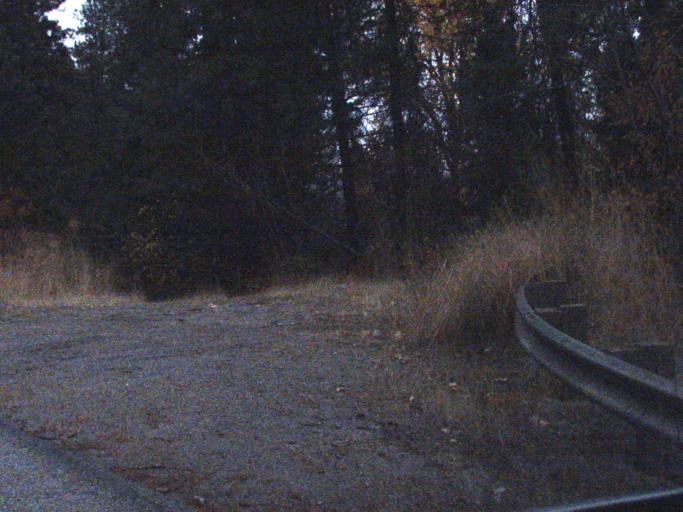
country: US
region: Washington
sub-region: Stevens County
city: Kettle Falls
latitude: 48.7407
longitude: -118.1343
